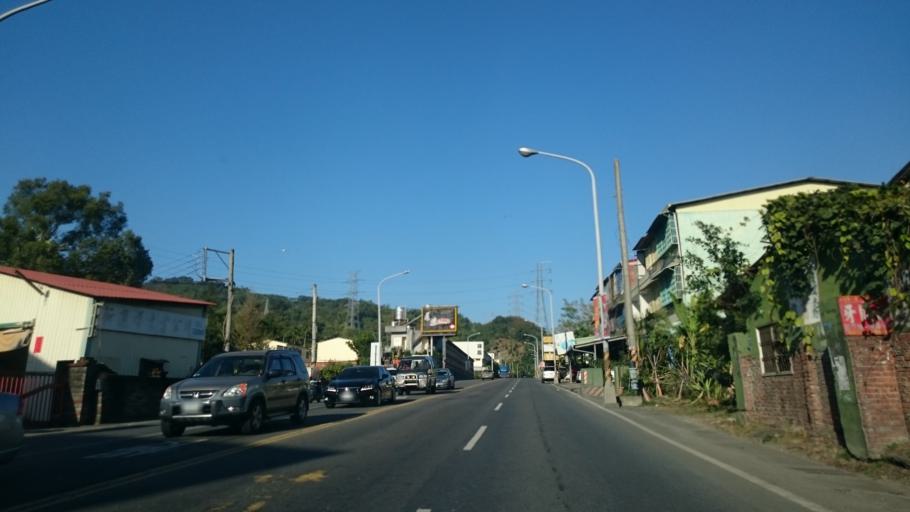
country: TW
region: Taiwan
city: Lugu
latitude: 23.8313
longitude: 120.7165
